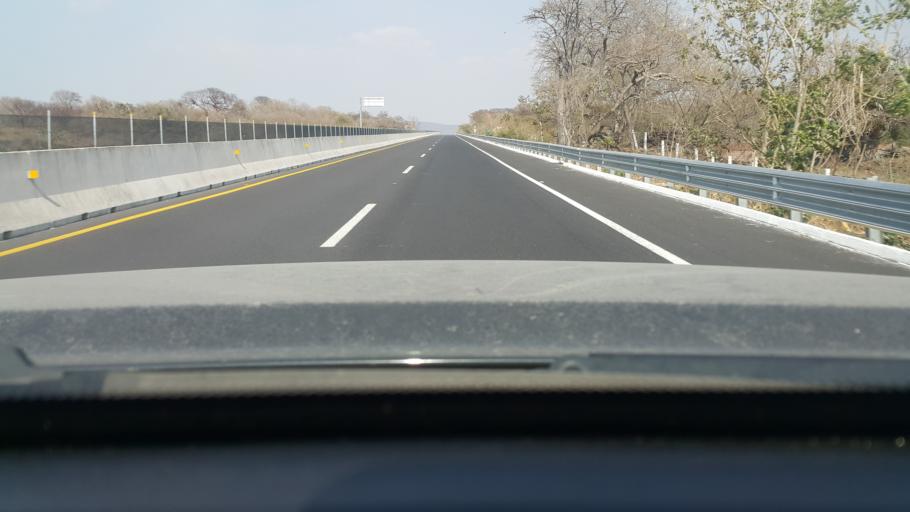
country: MX
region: Nayarit
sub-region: Ahuacatlan
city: Ahuacatlan
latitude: 21.0668
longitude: -104.4738
